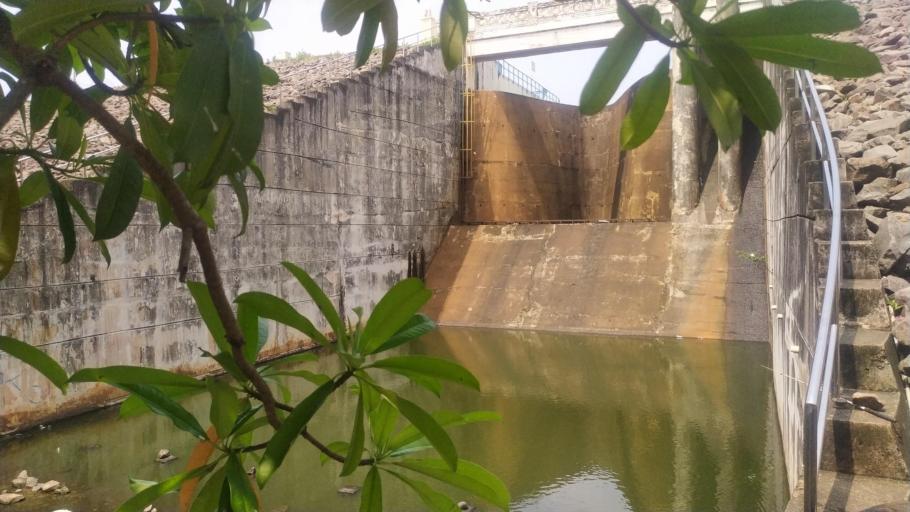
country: ID
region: Banten
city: South Tangerang
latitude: -6.3013
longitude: 106.7632
